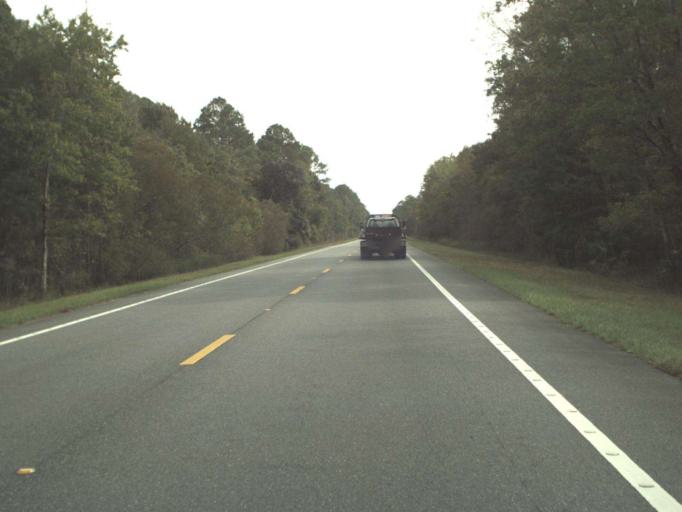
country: US
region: Florida
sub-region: Leon County
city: Woodville
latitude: 30.1725
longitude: -84.0083
